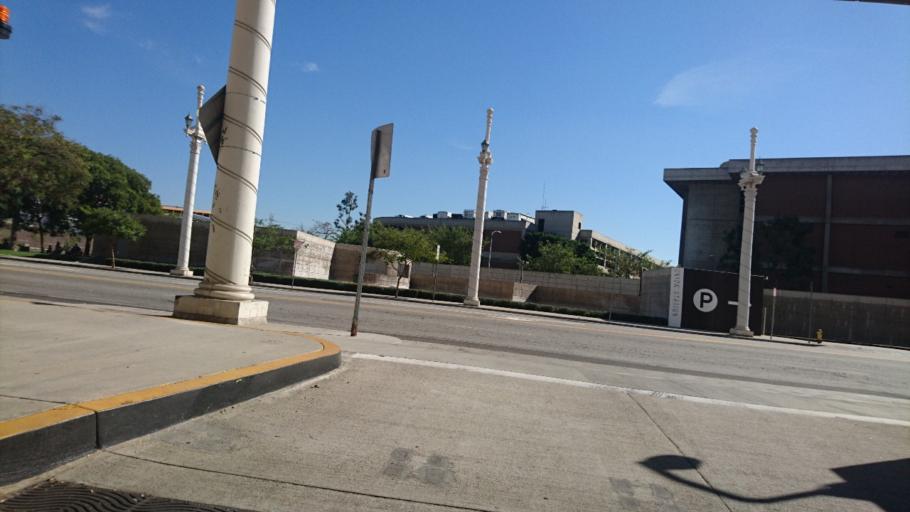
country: US
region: California
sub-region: Los Angeles County
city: Los Angeles
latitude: 34.0560
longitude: -118.2324
